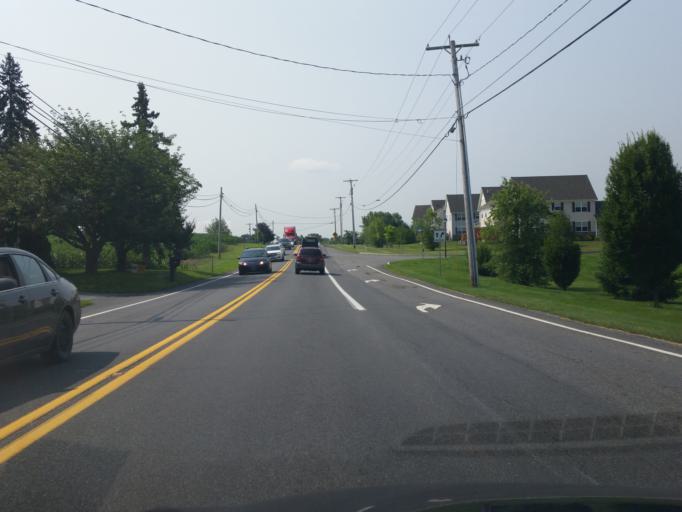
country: US
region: Pennsylvania
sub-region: Dauphin County
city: Palmdale
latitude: 40.3697
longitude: -76.6502
